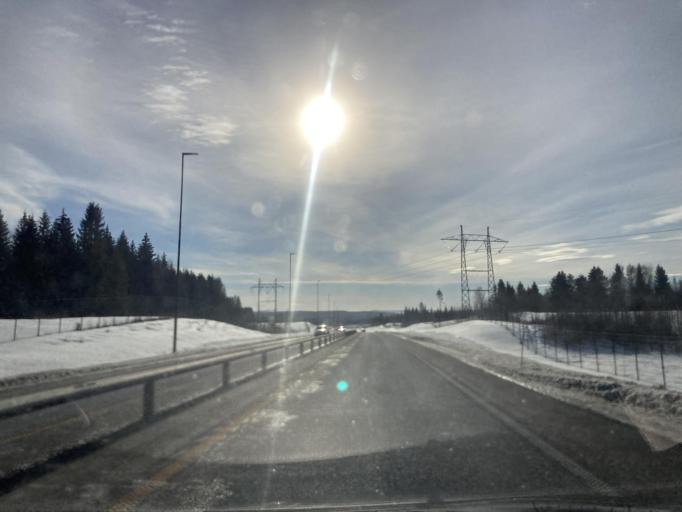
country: NO
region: Hedmark
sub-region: Loten
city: Loten
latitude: 60.8106
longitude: 11.2865
